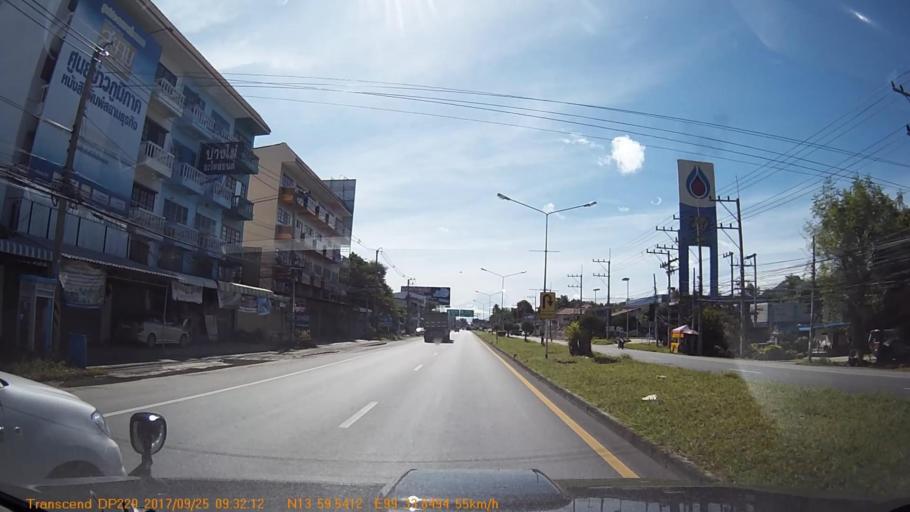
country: TH
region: Kanchanaburi
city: Kanchanaburi
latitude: 13.9922
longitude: 99.5644
